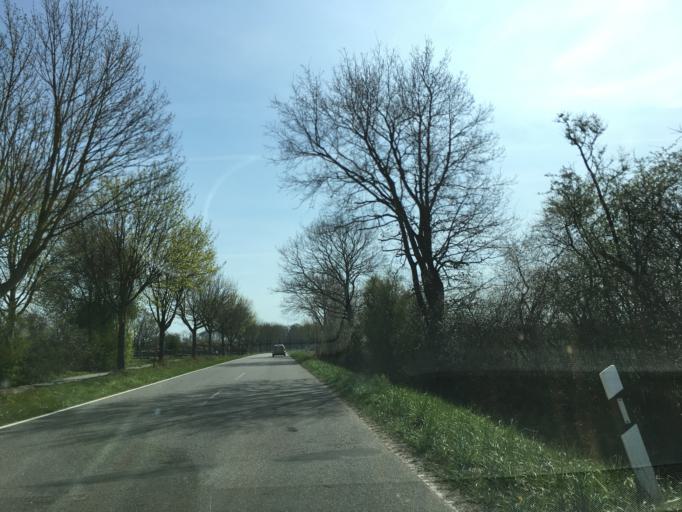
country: DE
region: Schleswig-Holstein
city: Felm
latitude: 54.3902
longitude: 10.0554
